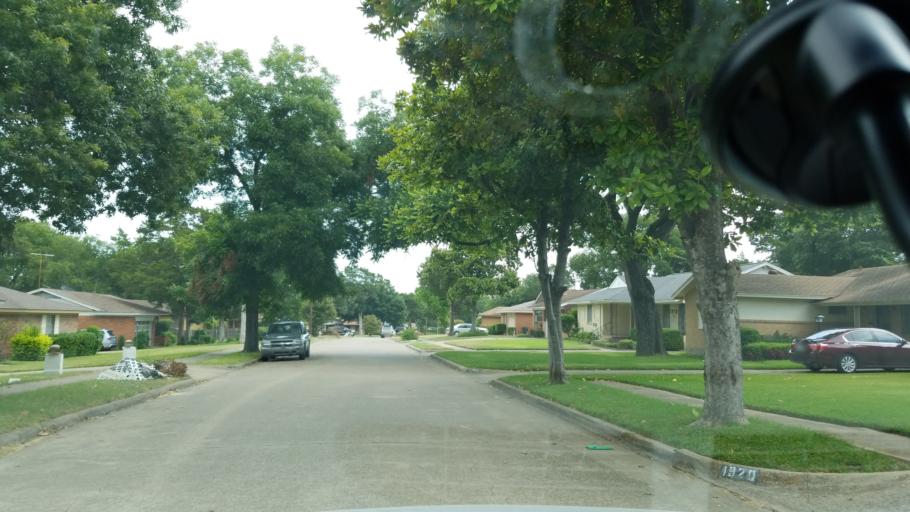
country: US
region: Texas
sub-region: Dallas County
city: Cockrell Hill
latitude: 32.6877
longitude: -96.8525
